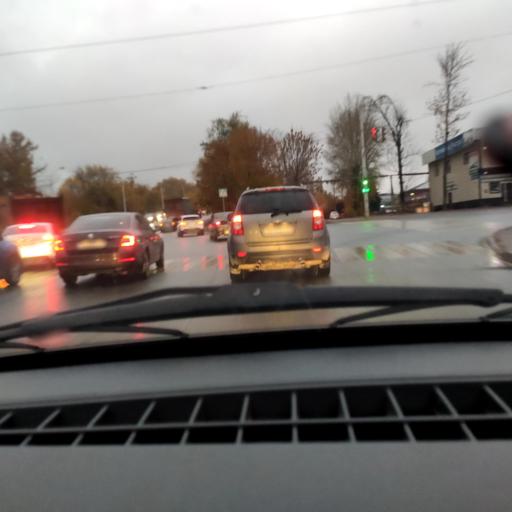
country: RU
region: Bashkortostan
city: Ufa
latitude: 54.8065
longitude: 56.0842
